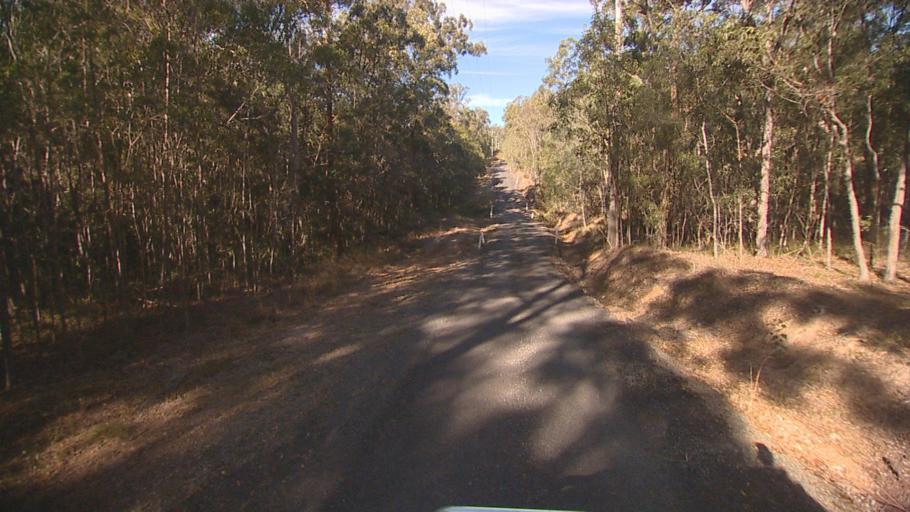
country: AU
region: Queensland
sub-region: Logan
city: Windaroo
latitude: -27.7893
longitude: 153.1715
